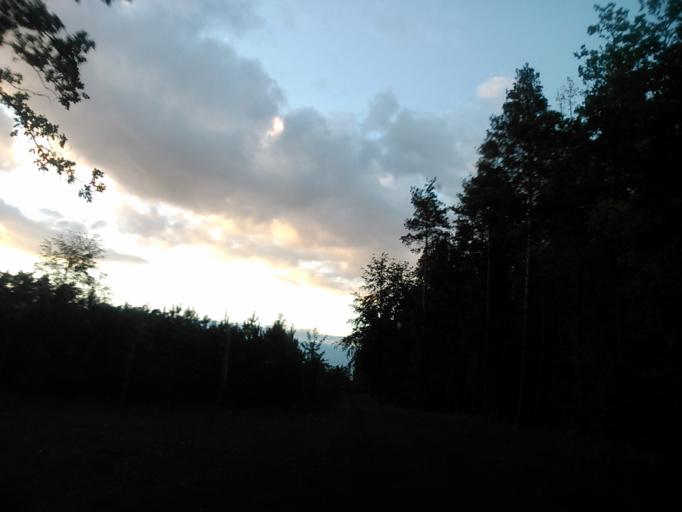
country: PL
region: Kujawsko-Pomorskie
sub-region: Powiat golubsko-dobrzynski
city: Radomin
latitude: 53.1641
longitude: 19.1389
